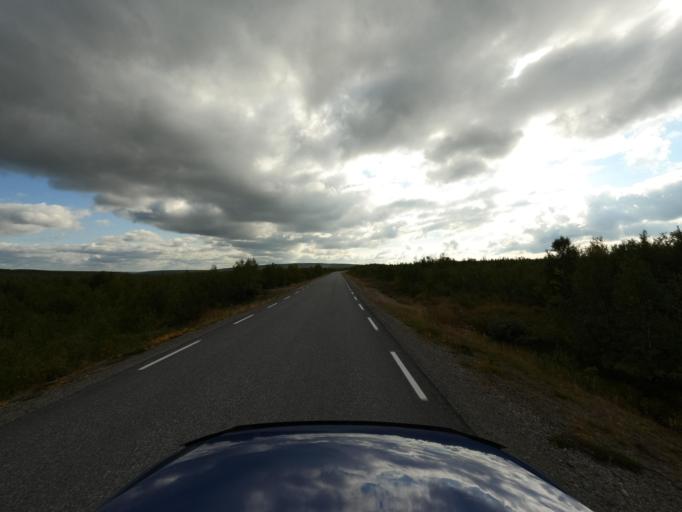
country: NO
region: Finnmark Fylke
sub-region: Porsanger
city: Lakselv
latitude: 69.3737
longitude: 24.2668
